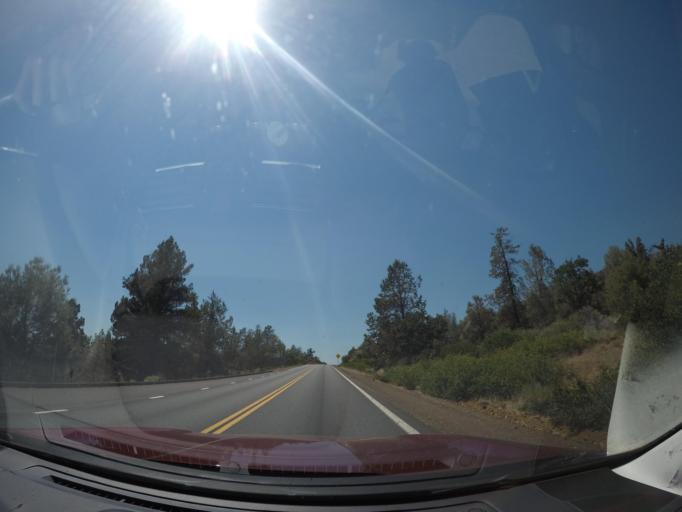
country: US
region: California
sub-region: Shasta County
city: Burney
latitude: 40.9924
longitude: -121.4746
